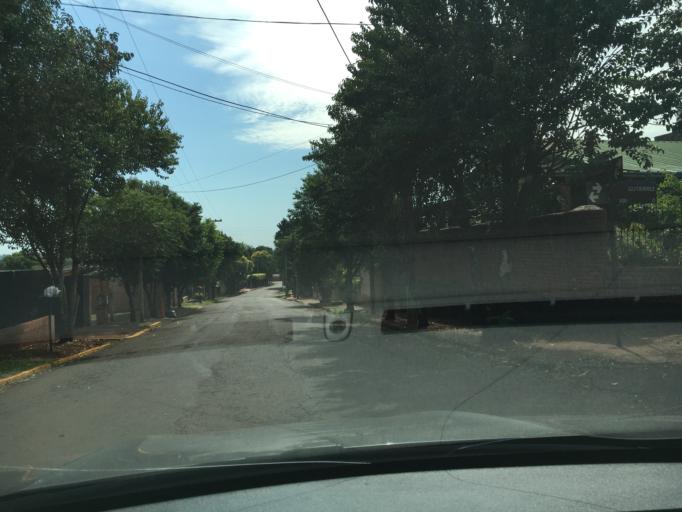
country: AR
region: Misiones
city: Puerto Rico
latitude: -26.8151
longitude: -55.0281
